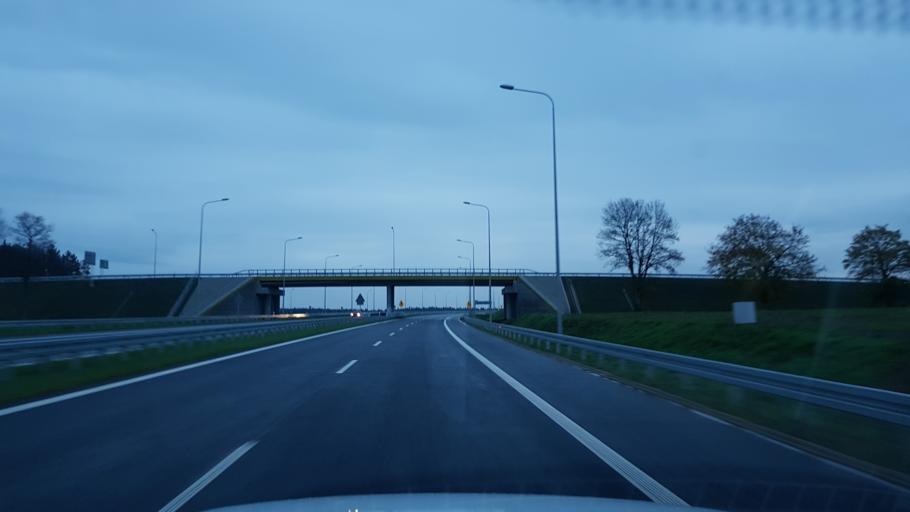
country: PL
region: West Pomeranian Voivodeship
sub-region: Powiat gryficki
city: Brojce
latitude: 53.9420
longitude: 15.3970
